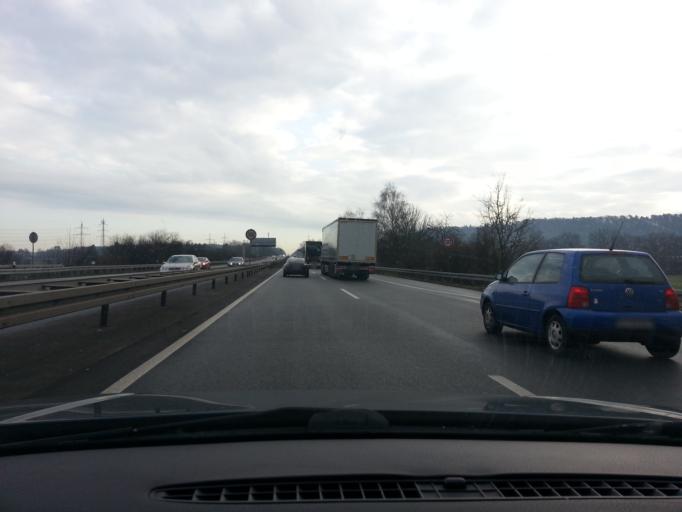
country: DE
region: Saarland
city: Kirkel
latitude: 49.3082
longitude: 7.2591
